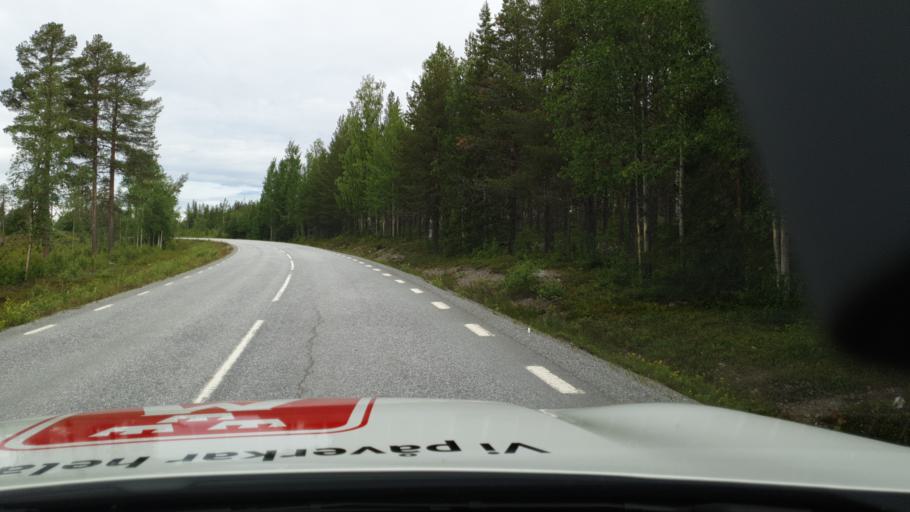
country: SE
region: Vaesterbotten
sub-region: Storumans Kommun
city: Storuman
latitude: 65.1384
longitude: 17.1037
